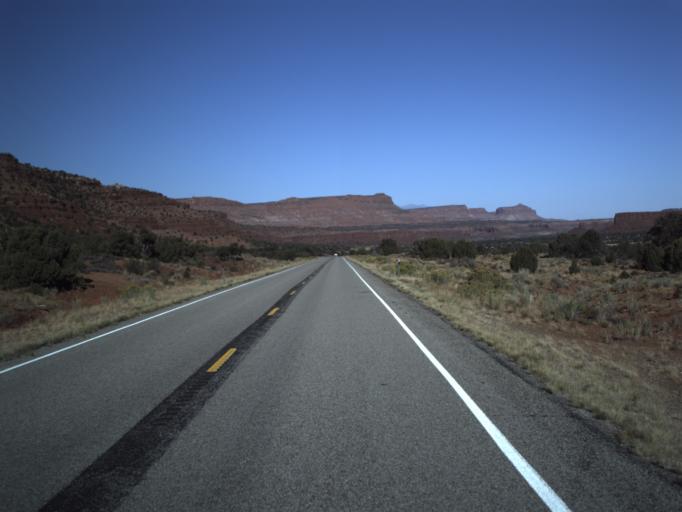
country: US
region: Utah
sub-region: San Juan County
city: Blanding
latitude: 37.6612
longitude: -110.1866
